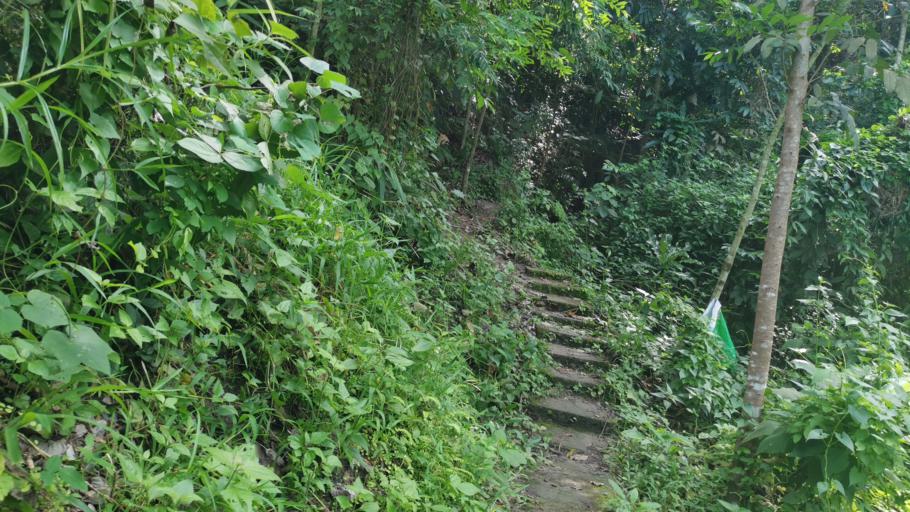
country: PH
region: Cordillera
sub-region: Province of Benguet
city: Bayabas
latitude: 16.4233
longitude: 120.5290
